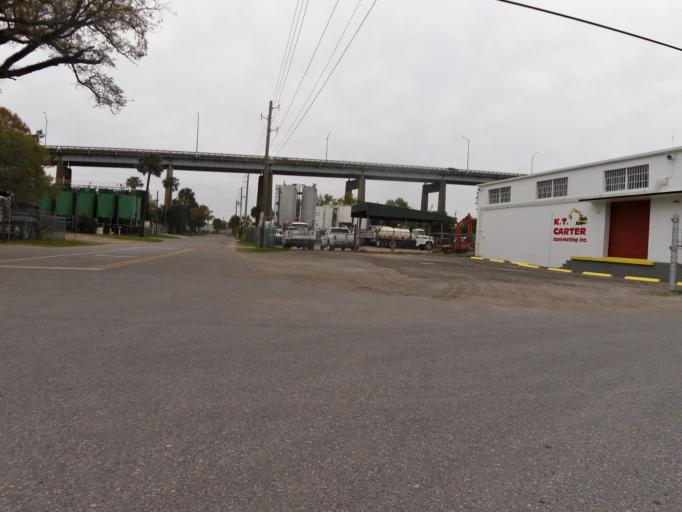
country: US
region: Florida
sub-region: Duval County
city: Jacksonville
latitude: 30.3258
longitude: -81.6307
